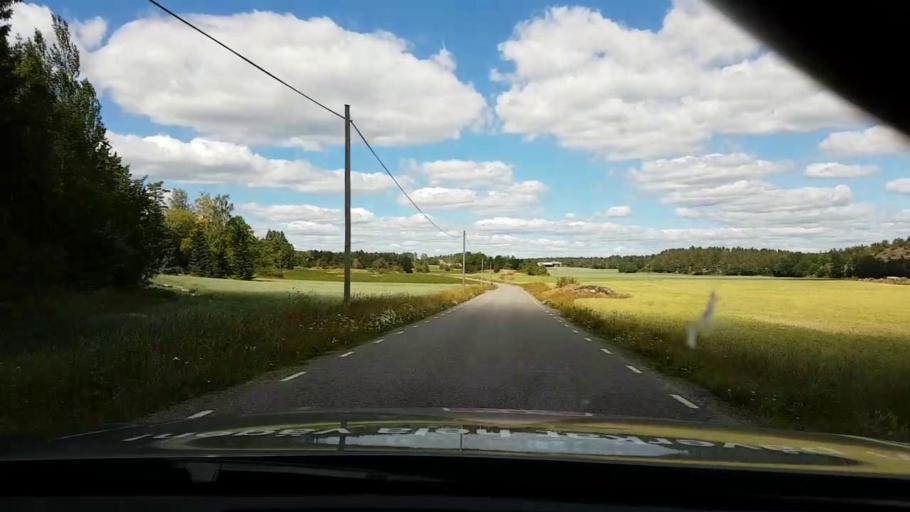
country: SE
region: Kalmar
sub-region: Vasterviks Kommun
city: Forserum
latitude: 58.0011
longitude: 16.5909
